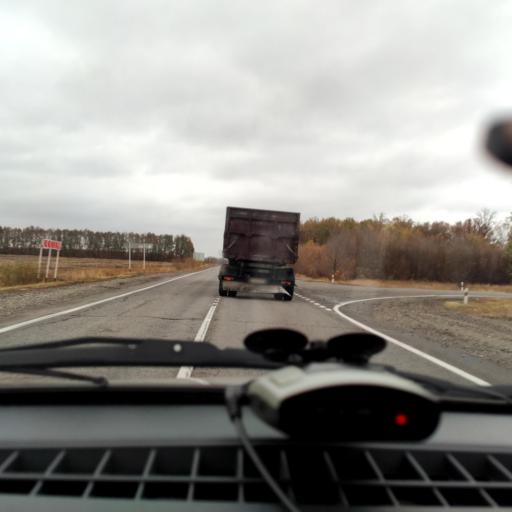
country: RU
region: Voronezj
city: Shilovo
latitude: 51.3954
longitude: 39.0029
